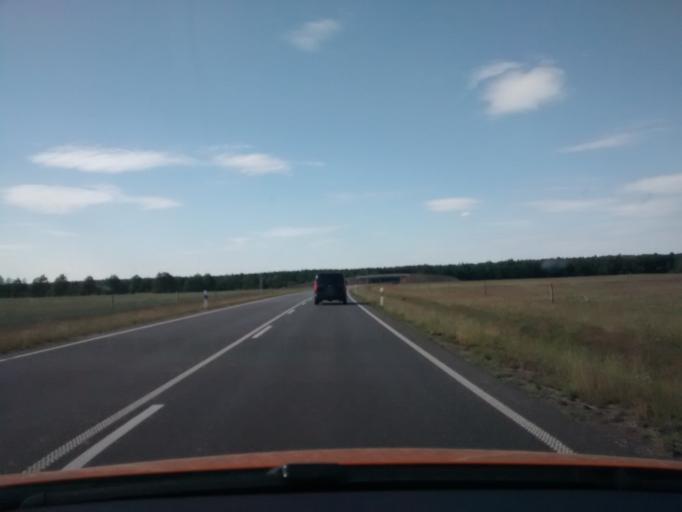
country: DE
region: Brandenburg
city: Juterbog
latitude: 52.0374
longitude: 13.1058
